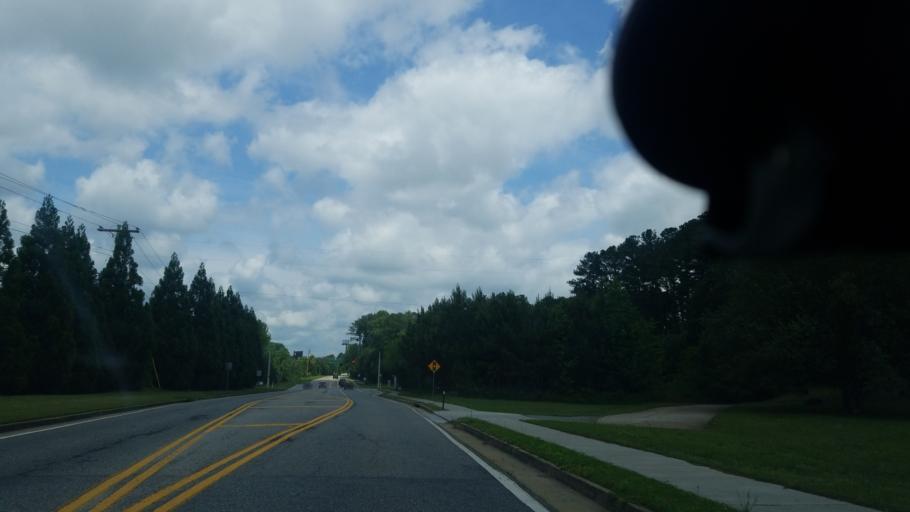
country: US
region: Georgia
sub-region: Forsyth County
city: Cumming
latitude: 34.1448
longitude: -84.1844
